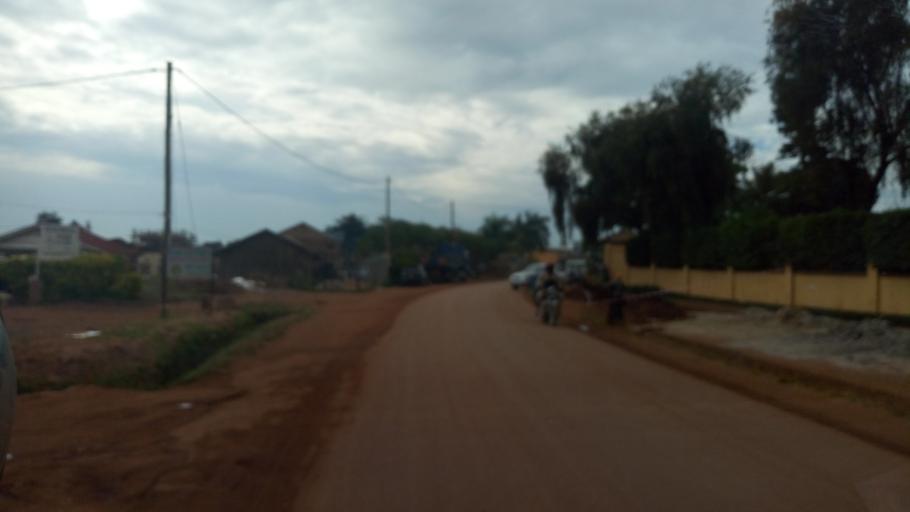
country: UG
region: Central Region
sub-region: Mukono District
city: Mukono
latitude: 0.3665
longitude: 32.7140
